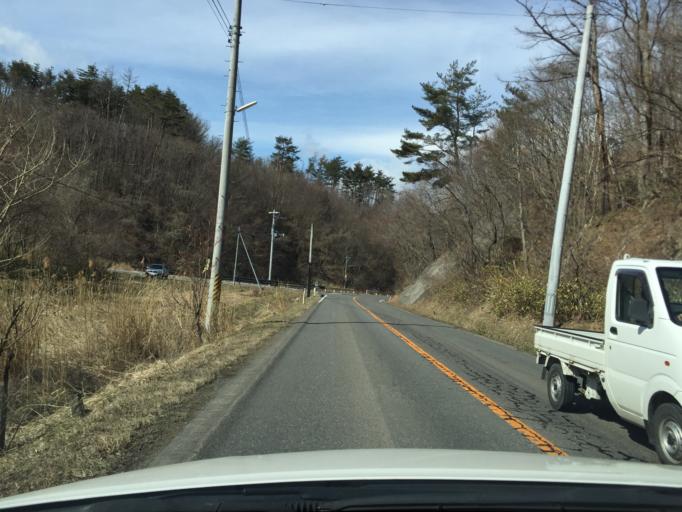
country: JP
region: Fukushima
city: Funehikimachi-funehiki
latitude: 37.4039
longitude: 140.5483
